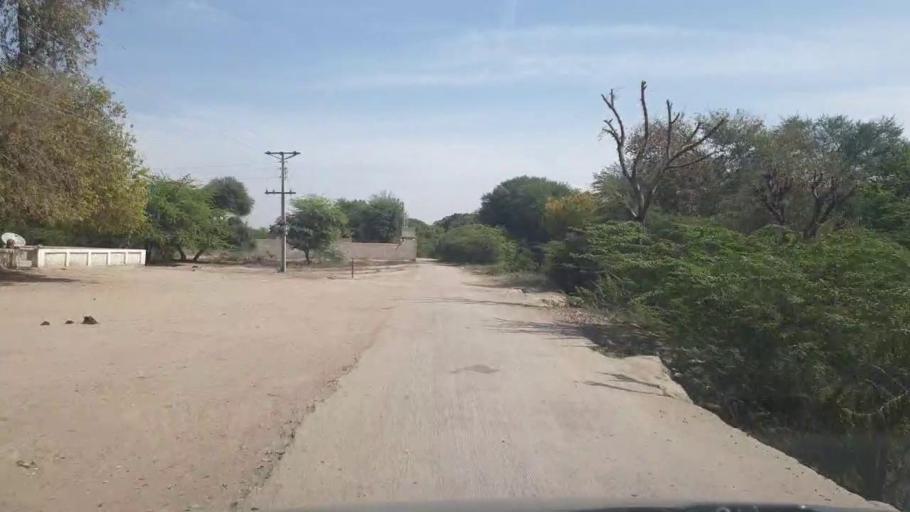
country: PK
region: Sindh
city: Kunri
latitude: 25.1893
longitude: 69.6871
